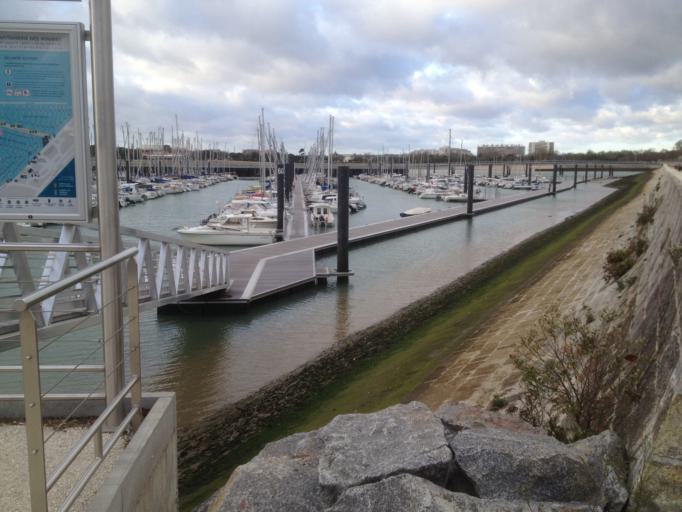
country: FR
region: Poitou-Charentes
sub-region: Departement de la Charente-Maritime
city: La Rochelle
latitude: 46.1488
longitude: -1.1609
